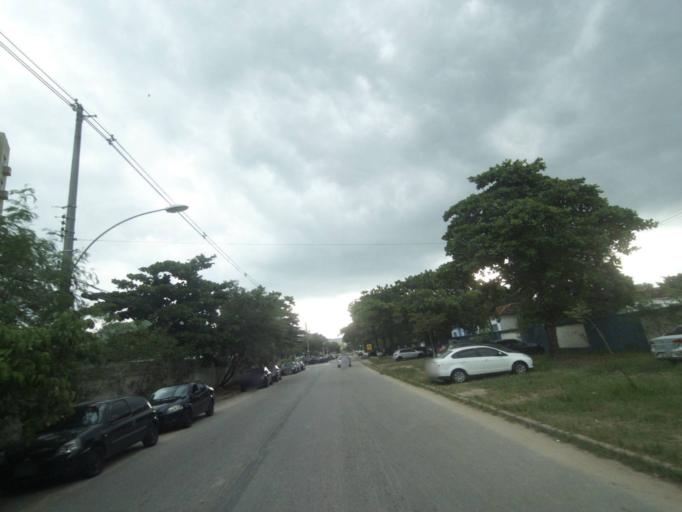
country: BR
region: Rio de Janeiro
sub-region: Nilopolis
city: Nilopolis
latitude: -22.8854
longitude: -43.3960
